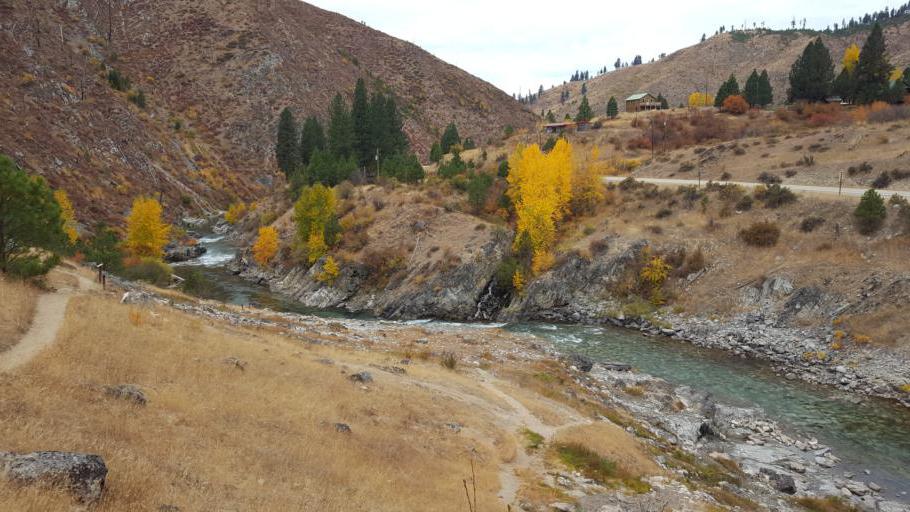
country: US
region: Idaho
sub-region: Boise County
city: Idaho City
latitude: 44.0725
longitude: -115.5454
